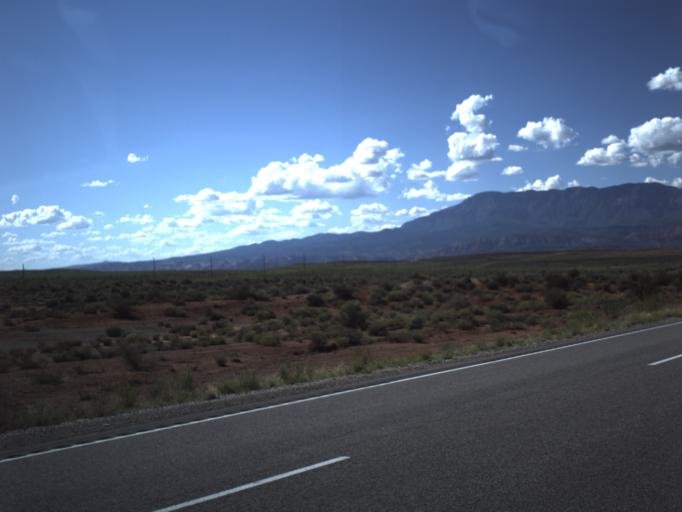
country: US
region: Utah
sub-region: Washington County
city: Hurricane
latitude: 37.1471
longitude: -113.2551
